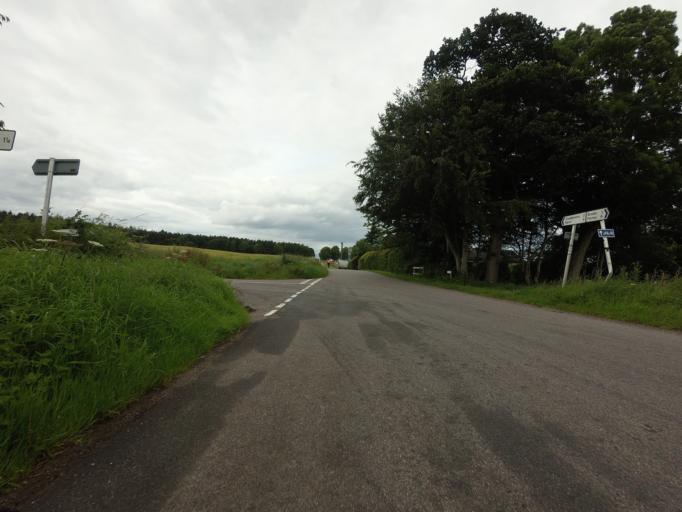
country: GB
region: Scotland
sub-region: Moray
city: Forres
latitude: 57.5996
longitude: -3.7206
